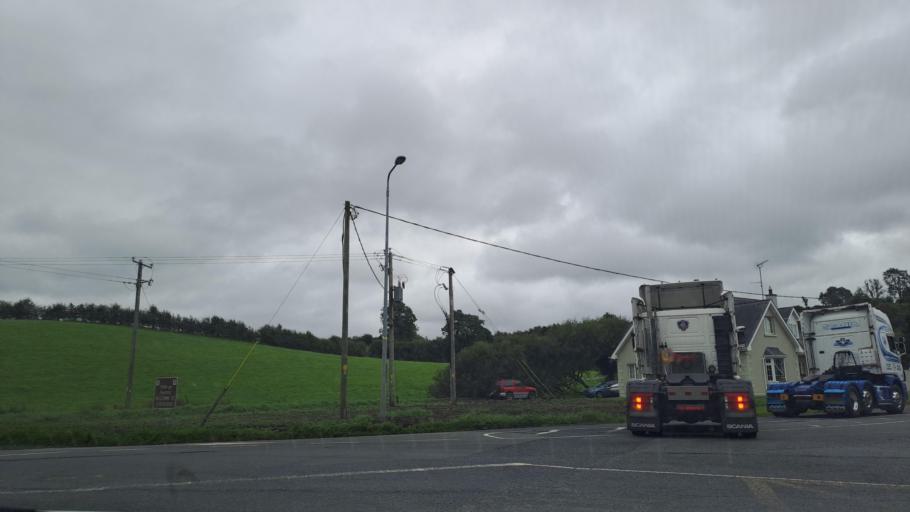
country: IE
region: Ulster
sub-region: An Cabhan
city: Bailieborough
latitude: 53.9983
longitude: -6.8912
